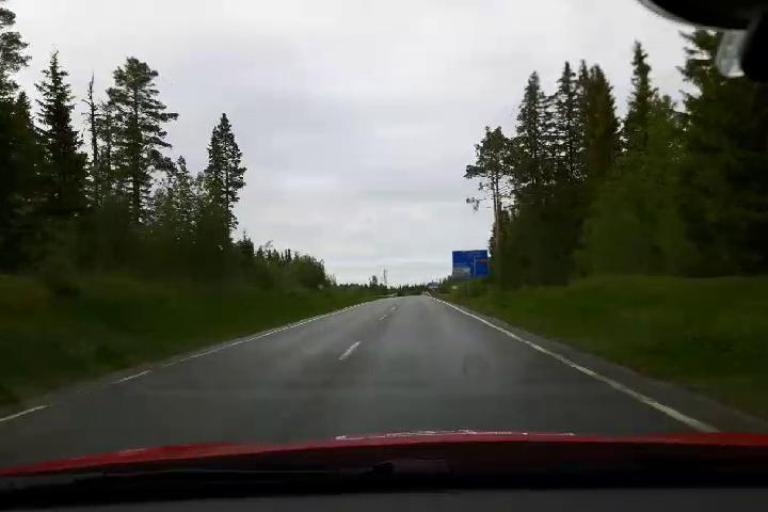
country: SE
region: Jaemtland
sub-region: Bergs Kommun
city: Hoverberg
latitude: 62.9133
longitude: 14.3291
